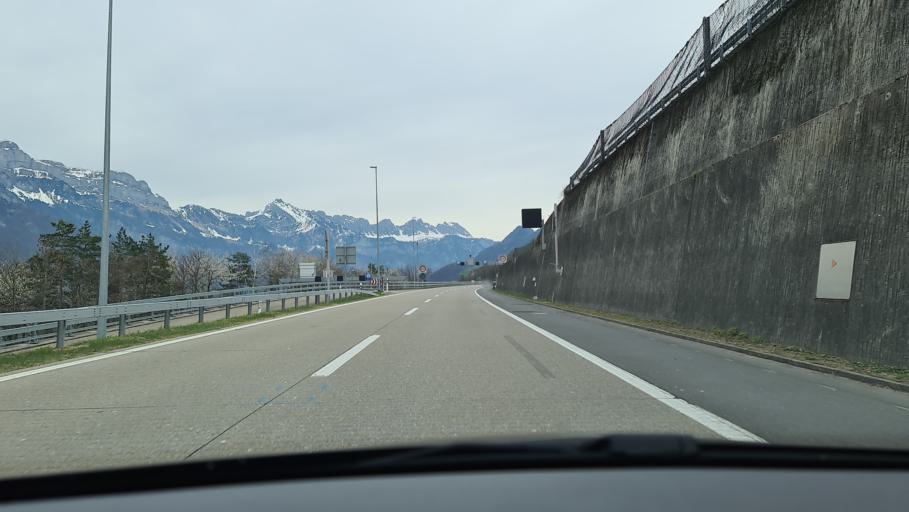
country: CH
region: Saint Gallen
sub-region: Wahlkreis Sarganserland
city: Quarten
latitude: 47.1132
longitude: 9.1983
